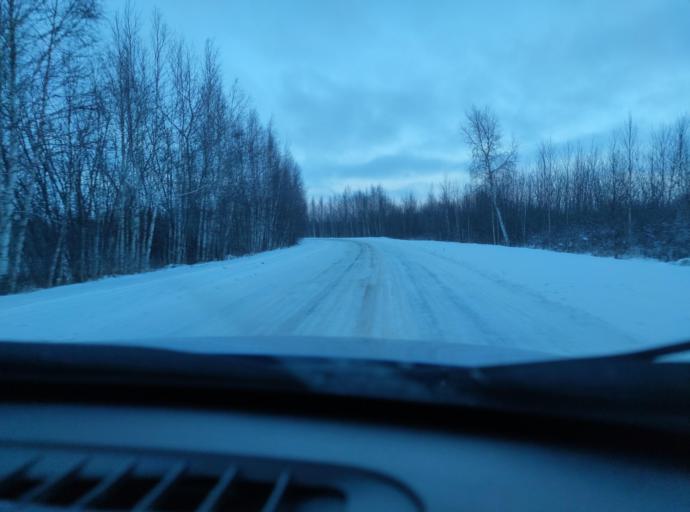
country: RU
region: Khanty-Mansiyskiy Avtonomnyy Okrug
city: Langepas
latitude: 61.1528
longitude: 75.1651
